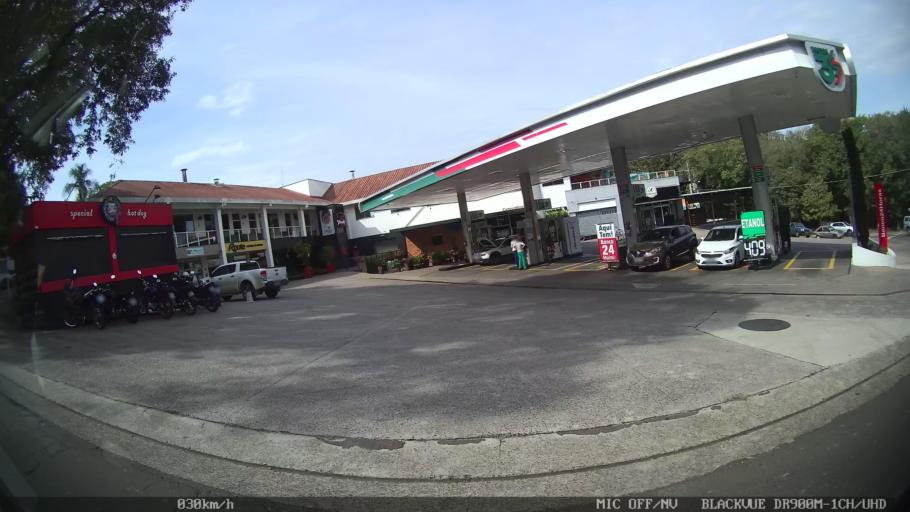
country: BR
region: Sao Paulo
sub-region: Piracicaba
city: Piracicaba
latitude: -22.7241
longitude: -47.6657
